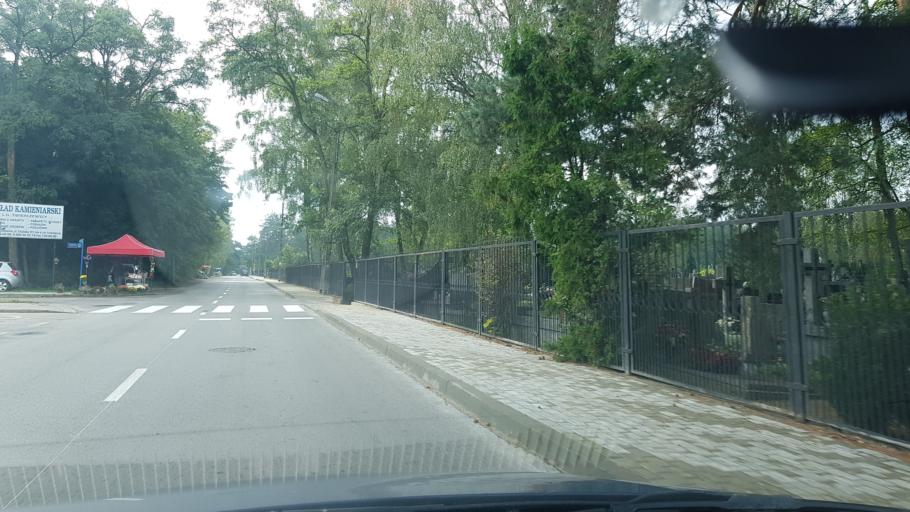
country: PL
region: Masovian Voivodeship
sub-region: Powiat piaseczynski
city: Konstancin-Jeziorna
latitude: 52.0675
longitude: 21.0996
